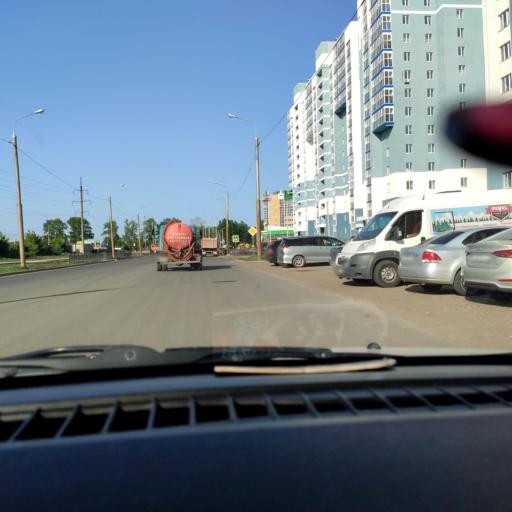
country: RU
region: Bashkortostan
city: Sterlitamak
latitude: 53.6396
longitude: 55.8951
